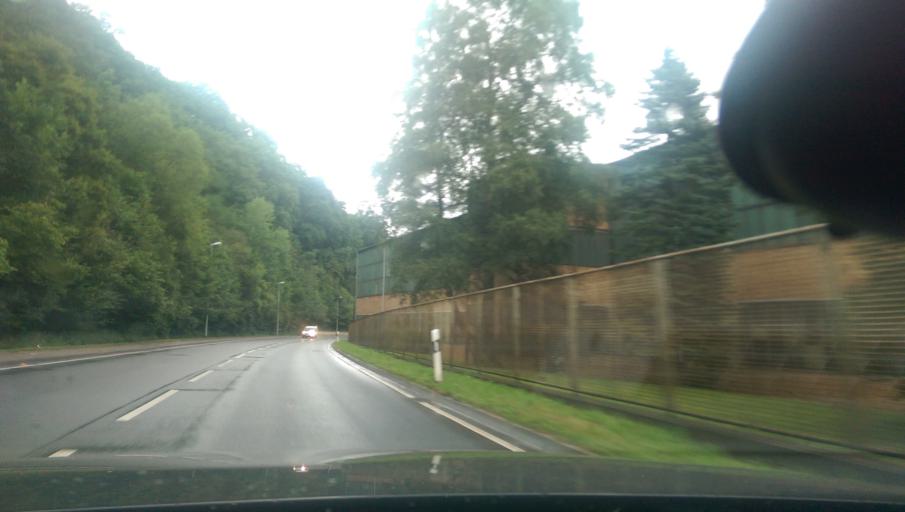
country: DE
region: Hesse
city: Witzenhausen
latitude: 51.3303
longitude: 9.8539
